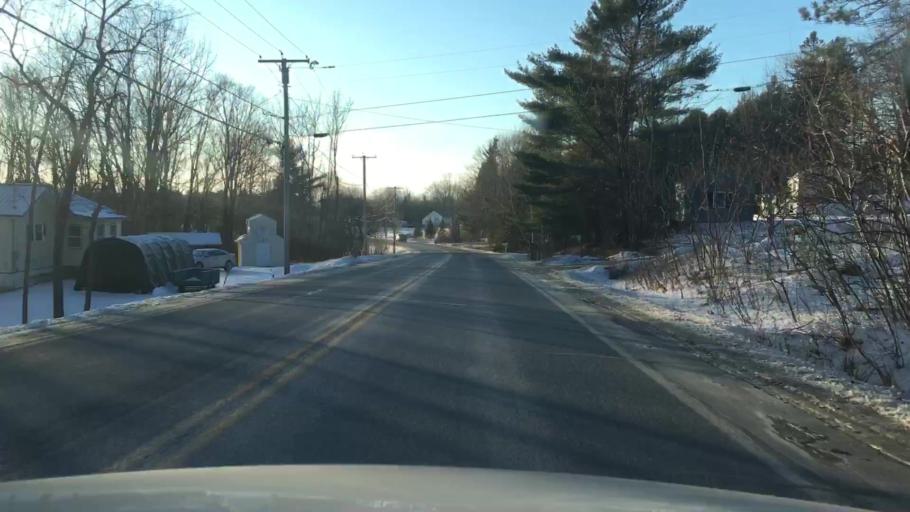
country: US
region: Maine
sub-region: Penobscot County
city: Eddington
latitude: 44.8298
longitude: -68.6701
